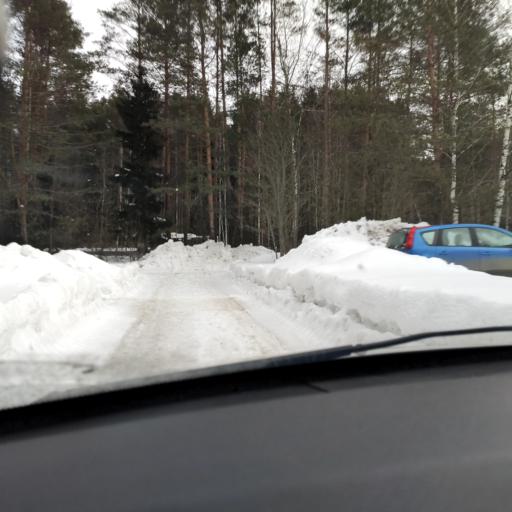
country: RU
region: Perm
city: Perm
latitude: 58.0545
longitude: 56.2252
